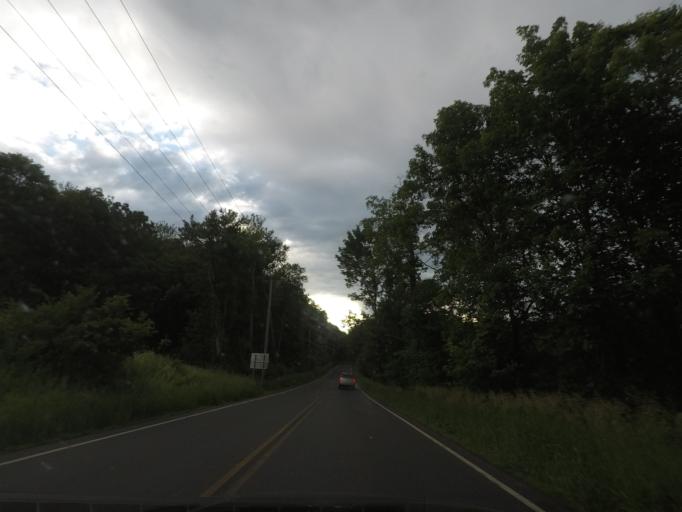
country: US
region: New York
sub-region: Dutchess County
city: Pine Plains
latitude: 41.9891
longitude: -73.6836
